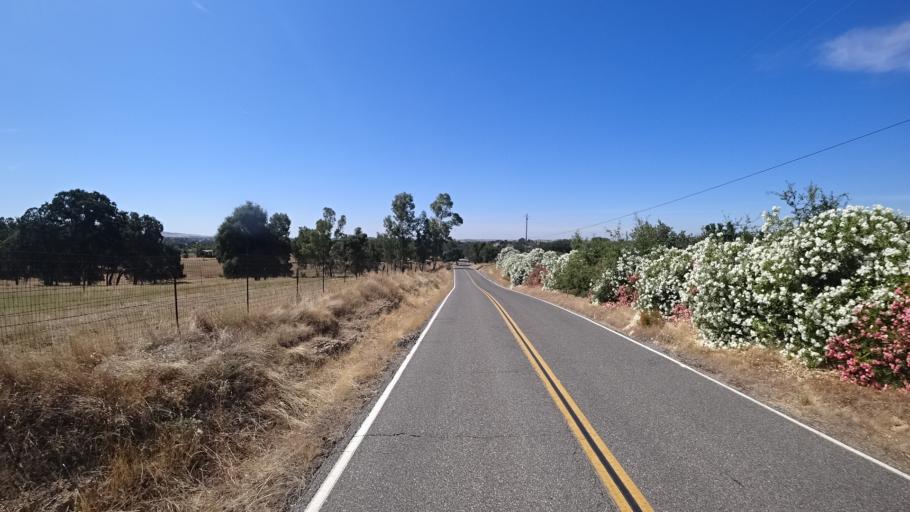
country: US
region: California
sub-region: Calaveras County
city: Rancho Calaveras
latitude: 38.1239
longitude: -120.9086
